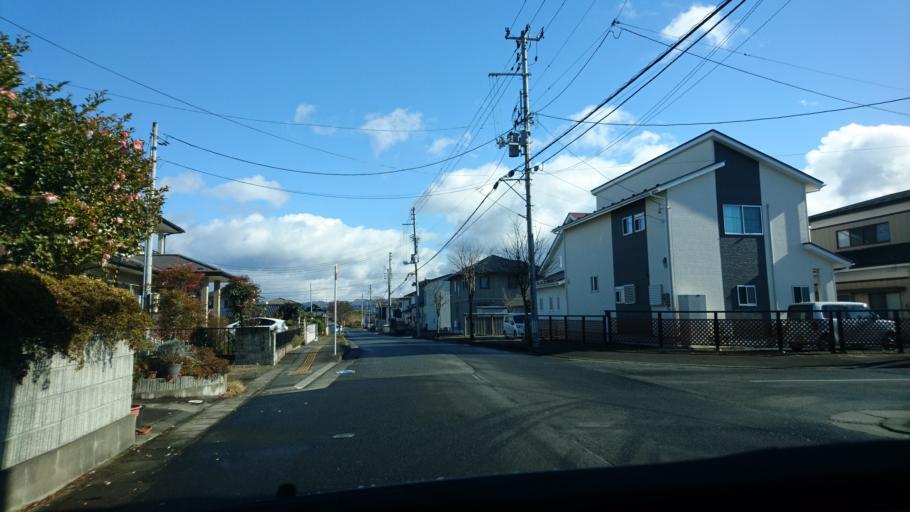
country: JP
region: Iwate
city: Ichinoseki
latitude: 38.9466
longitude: 141.1308
